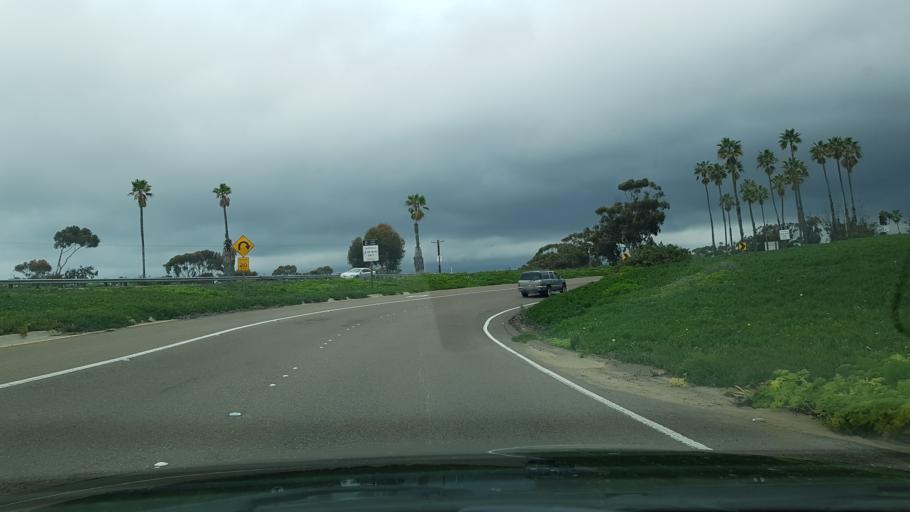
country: US
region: California
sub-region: San Diego County
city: Oceanside
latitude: 33.2099
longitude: -117.3884
